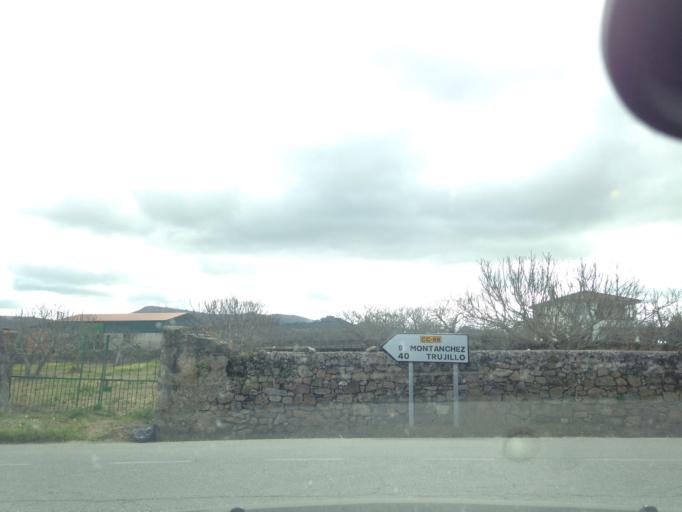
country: ES
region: Extremadura
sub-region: Provincia de Caceres
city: Albala
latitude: 39.2575
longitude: -6.1813
